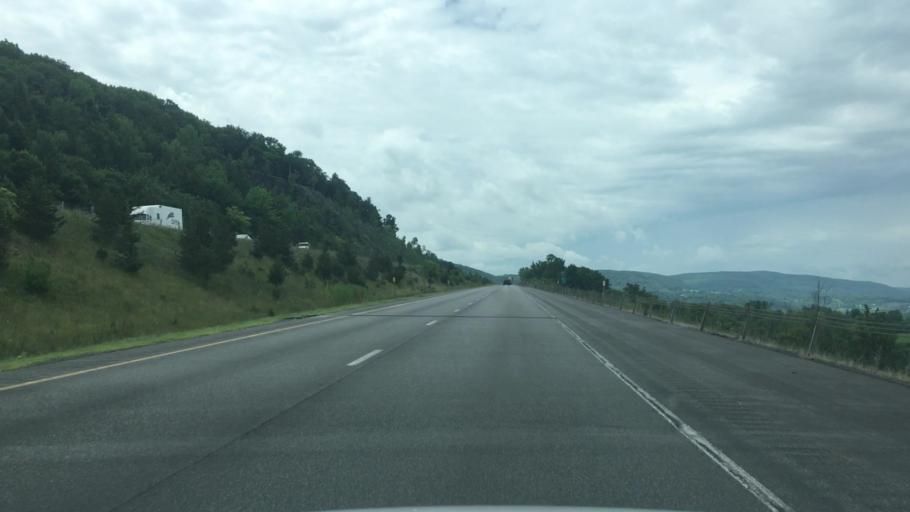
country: US
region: New York
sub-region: Schoharie County
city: Schoharie
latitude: 42.6979
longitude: -74.3456
